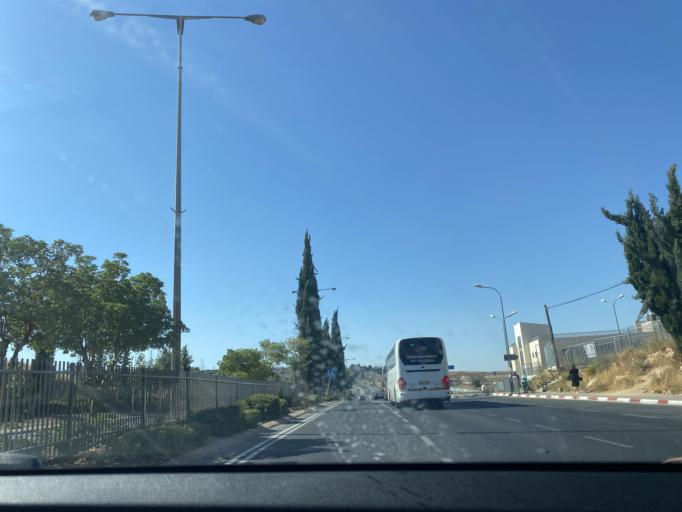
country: PS
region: West Bank
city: Bayt Iksa
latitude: 31.8229
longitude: 35.1893
